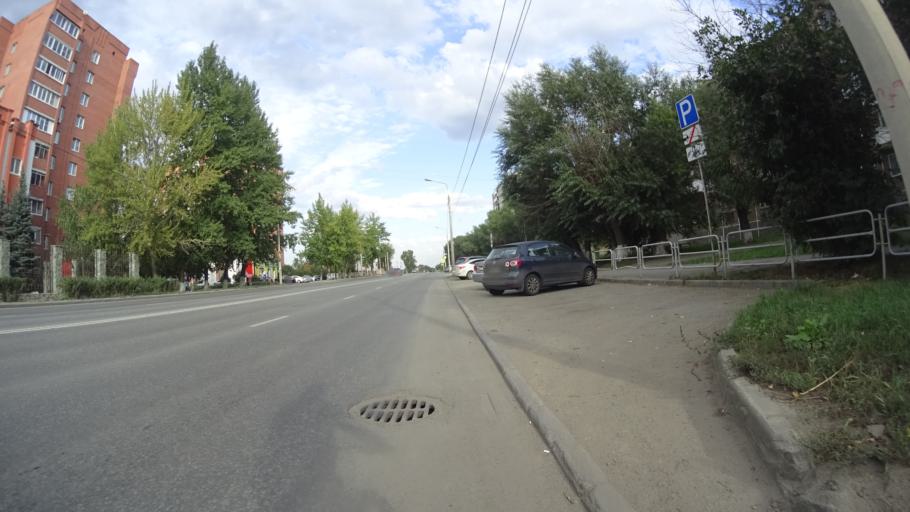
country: RU
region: Chelyabinsk
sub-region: Gorod Chelyabinsk
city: Chelyabinsk
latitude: 55.1985
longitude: 61.3359
